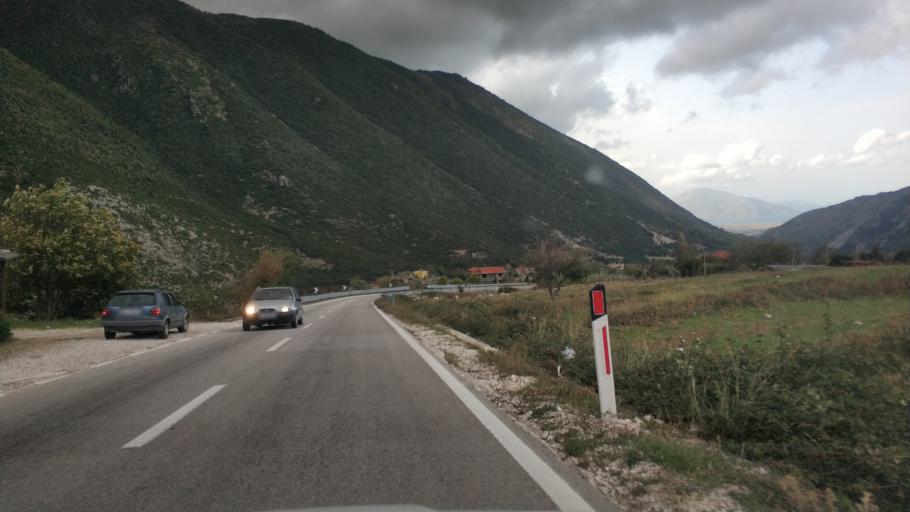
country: AL
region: Vlore
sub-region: Rrethi i Vlores
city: Brataj
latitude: 40.2321
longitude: 19.5640
